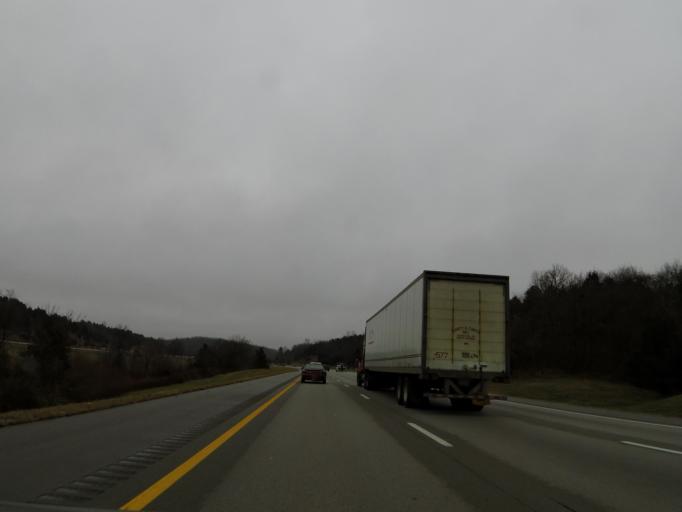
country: US
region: Kentucky
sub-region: Scott County
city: Georgetown
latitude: 38.3393
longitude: -84.5682
